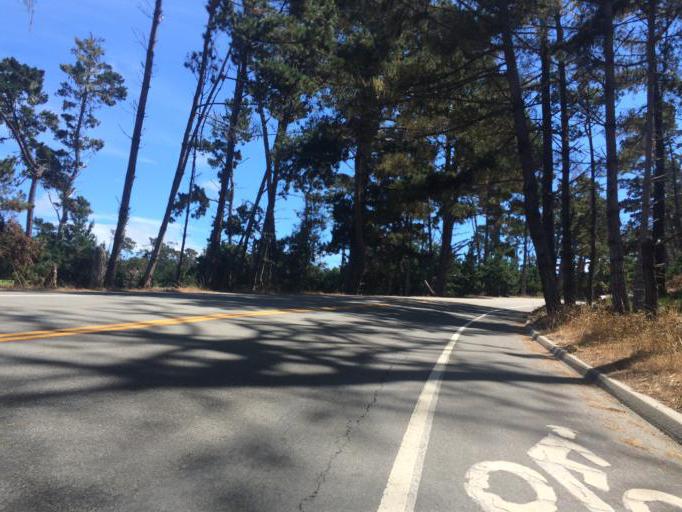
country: US
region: California
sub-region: Monterey County
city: Del Monte Forest
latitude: 36.5848
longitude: -121.9596
